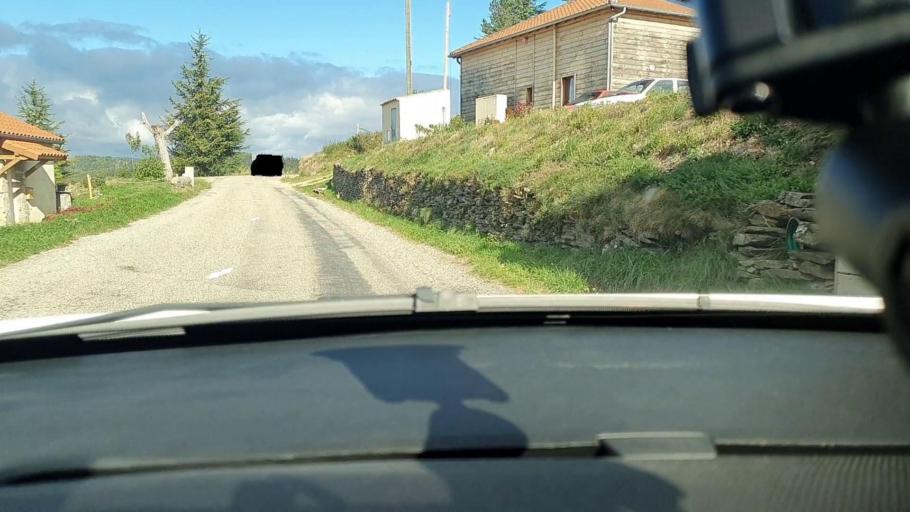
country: FR
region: Rhone-Alpes
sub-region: Departement de l'Ardeche
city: Les Vans
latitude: 44.4157
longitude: 4.0223
